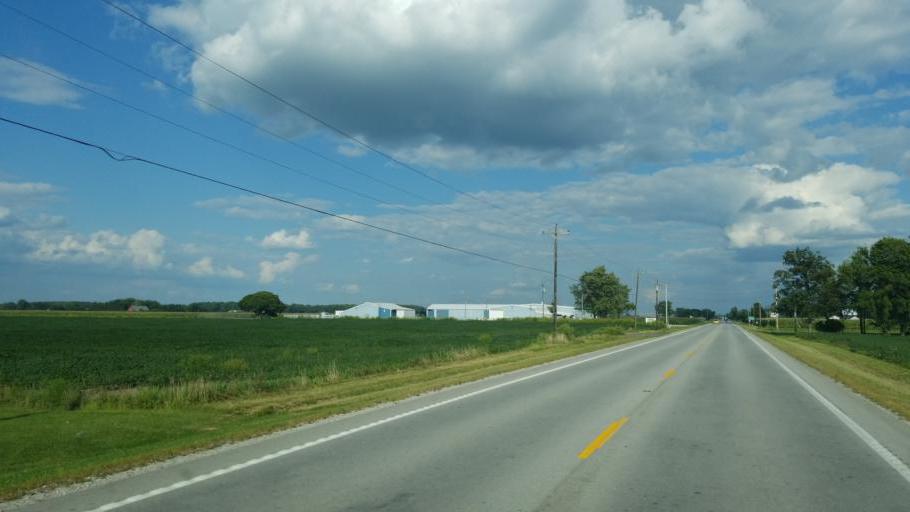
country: US
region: Ohio
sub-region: Wood County
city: Bowling Green
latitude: 41.3620
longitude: -83.5550
